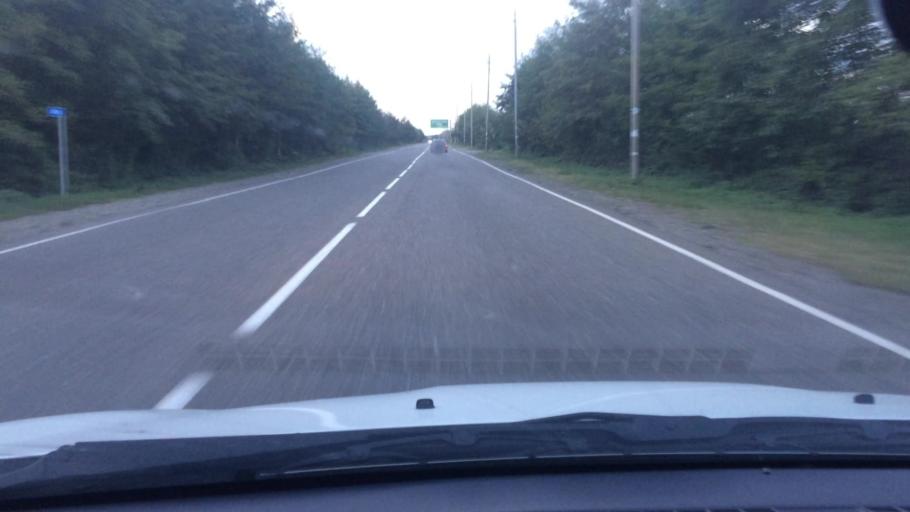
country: GE
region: Guria
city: Urek'i
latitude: 41.9312
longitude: 41.7725
